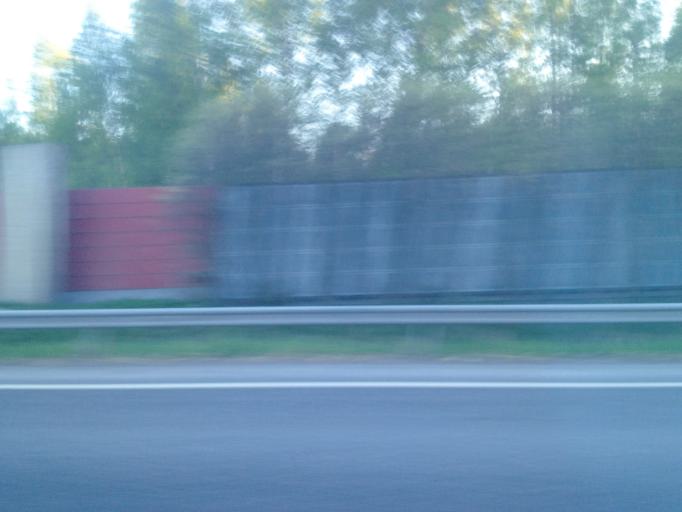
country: FI
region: Haeme
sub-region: Haemeenlinna
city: Haemeenlinna
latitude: 60.9759
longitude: 24.4710
